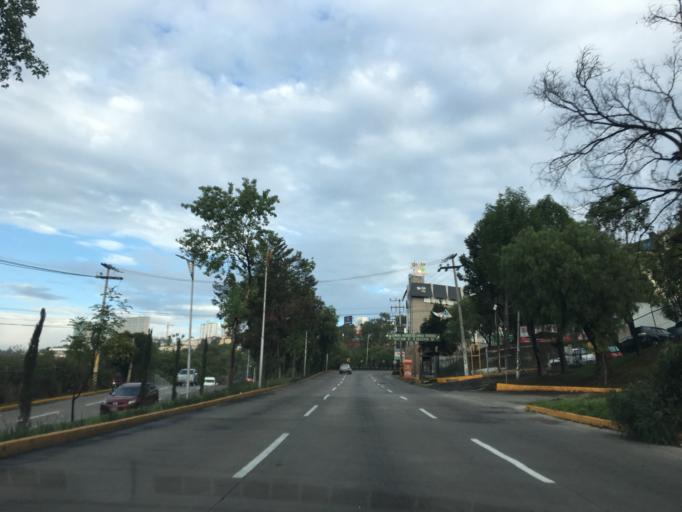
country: MX
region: Mexico
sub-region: Naucalpan de Juarez
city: Ejido del Tejocote
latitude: 19.5121
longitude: -99.2633
